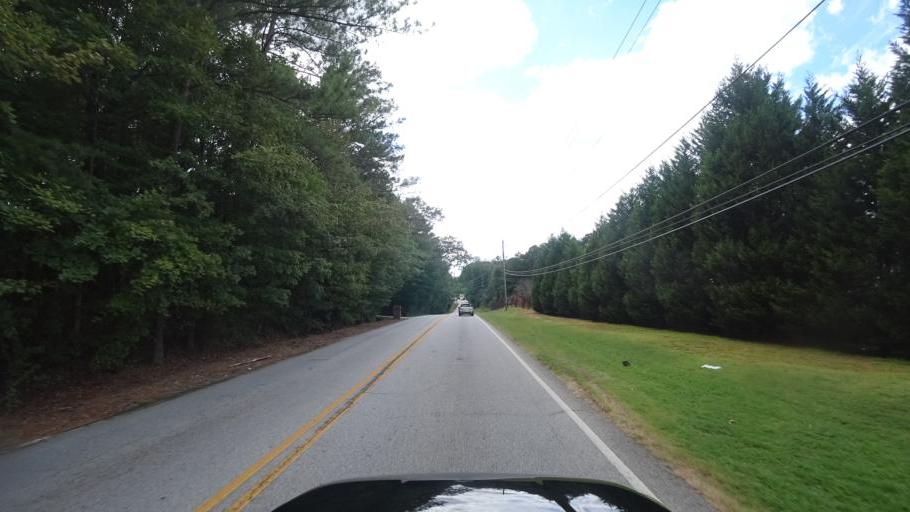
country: US
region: Georgia
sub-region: DeKalb County
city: Panthersville
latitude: 33.6561
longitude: -84.2167
